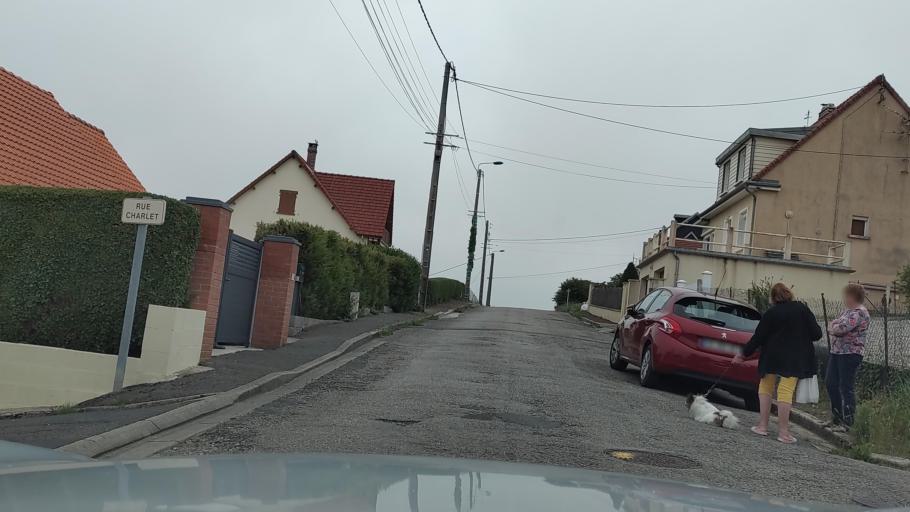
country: FR
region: Picardie
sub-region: Departement de la Somme
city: Ault
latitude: 50.0987
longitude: 1.4456
